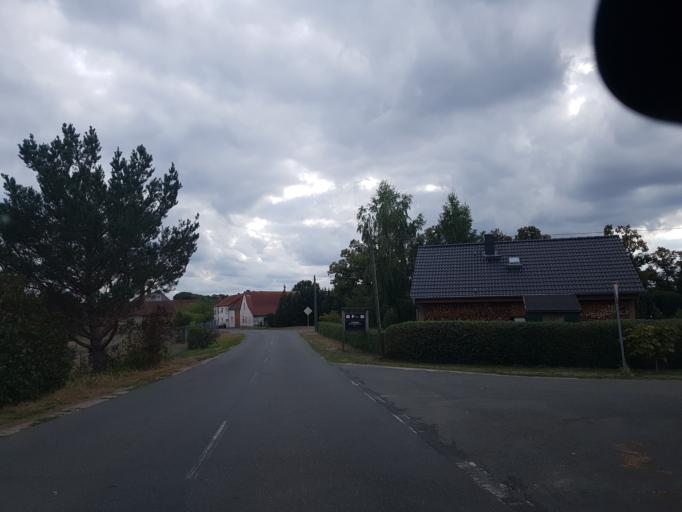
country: DE
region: Saxony-Anhalt
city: Rosslau
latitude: 51.9599
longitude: 12.3011
